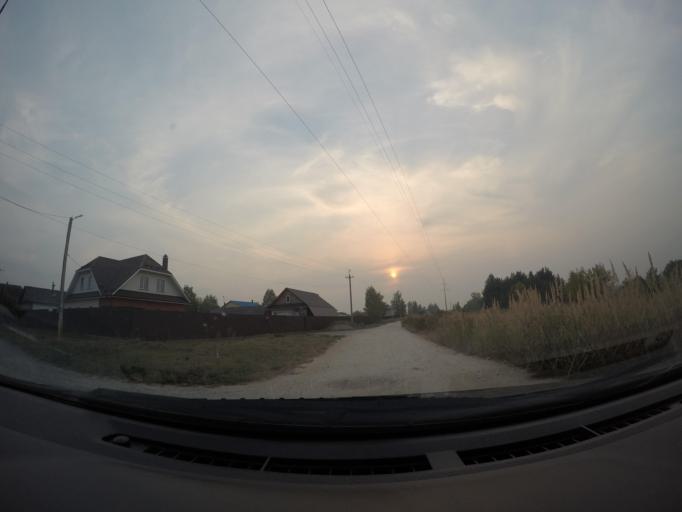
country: RU
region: Moskovskaya
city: Imeni Tsyurupy
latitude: 55.4995
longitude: 38.6635
